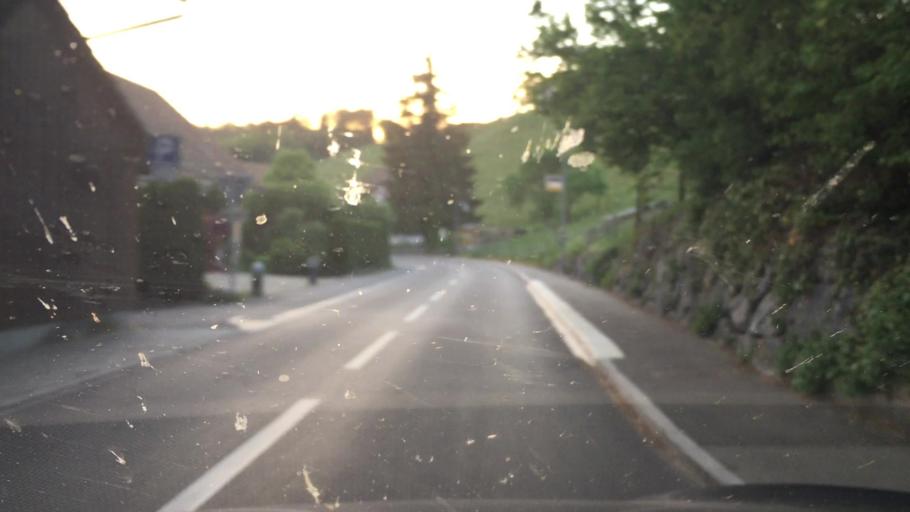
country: CH
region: Thurgau
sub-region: Frauenfeld District
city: Huttwilen
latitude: 47.5837
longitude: 8.8728
